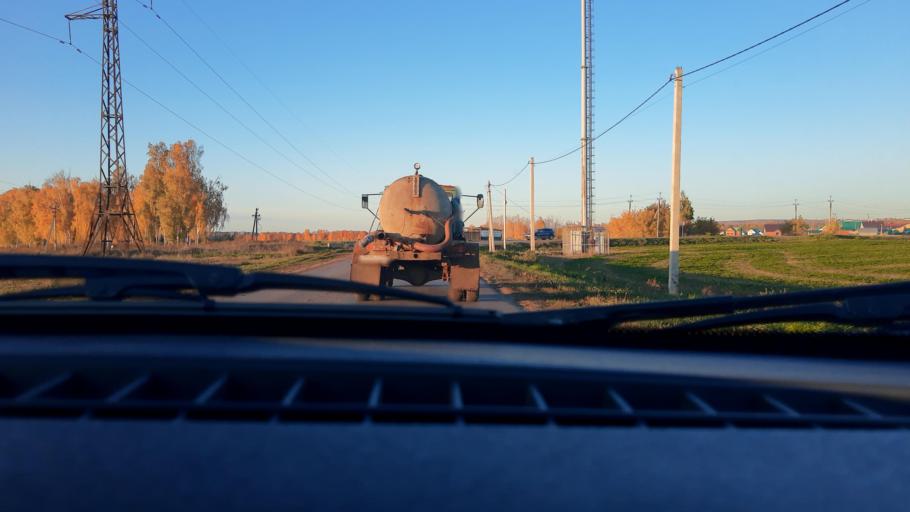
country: RU
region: Bashkortostan
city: Ufa
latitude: 54.8456
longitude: 56.0006
